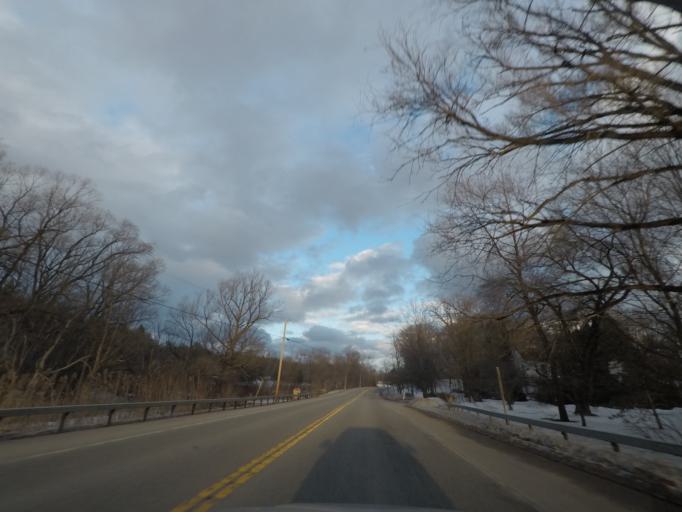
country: US
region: New York
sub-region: Montgomery County
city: Saint Johnsville
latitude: 43.0052
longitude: -74.7291
